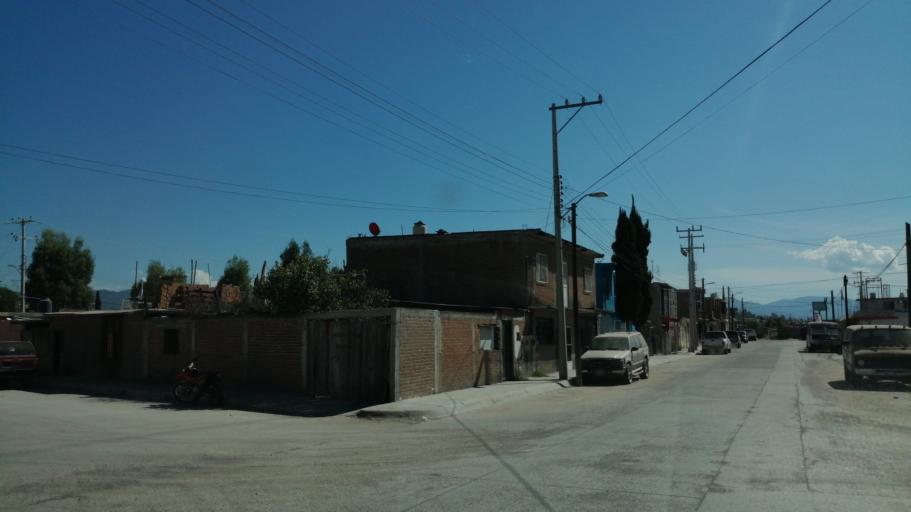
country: MX
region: Durango
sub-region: Santiago Papasquiaro
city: Santiago Papasquiaro
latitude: 25.0491
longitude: -105.4363
